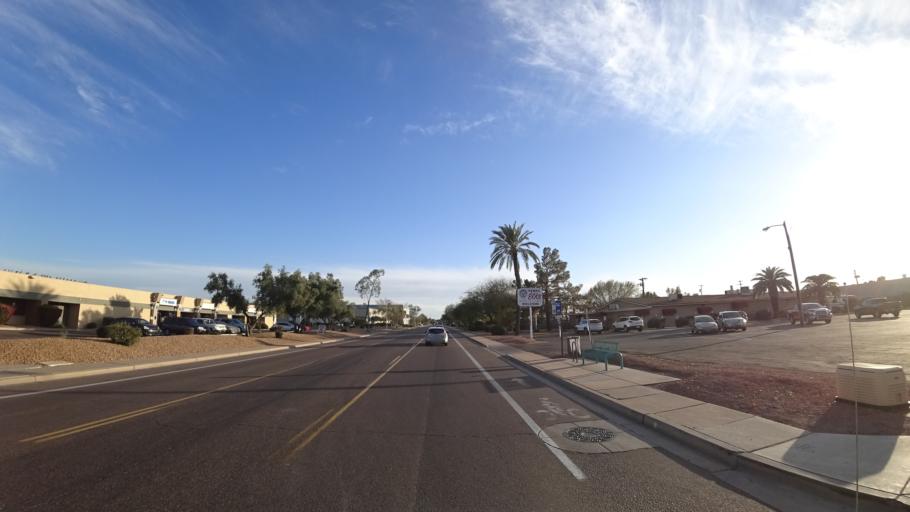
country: US
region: Arizona
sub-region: Maricopa County
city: Tempe Junction
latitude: 33.4037
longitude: -111.9522
